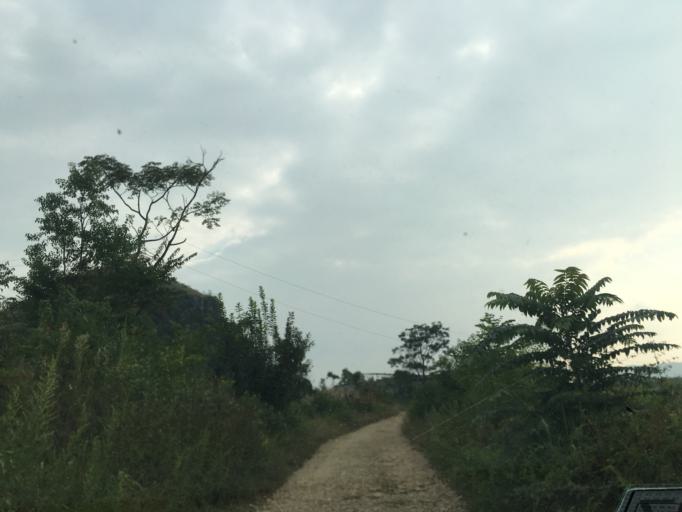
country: CN
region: Guangxi Zhuangzu Zizhiqu
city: Xinzhou
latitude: 25.4450
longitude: 105.6446
